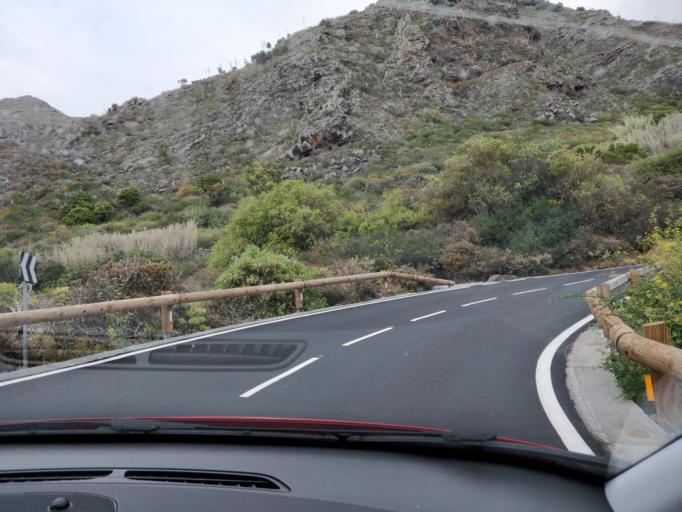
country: ES
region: Canary Islands
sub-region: Provincia de Santa Cruz de Tenerife
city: Tanque
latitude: 28.3546
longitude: -16.8441
